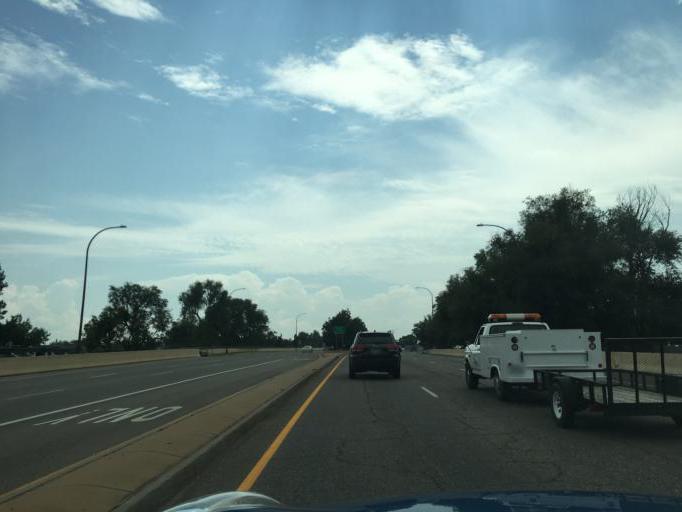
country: US
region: Colorado
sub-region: Jefferson County
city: Arvada
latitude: 39.8051
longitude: -105.0773
